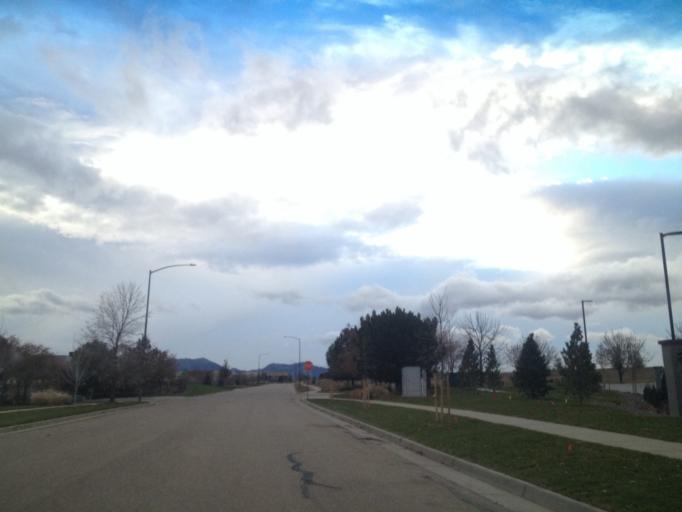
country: US
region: Colorado
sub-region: Boulder County
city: Louisville
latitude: 39.9709
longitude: -105.1119
